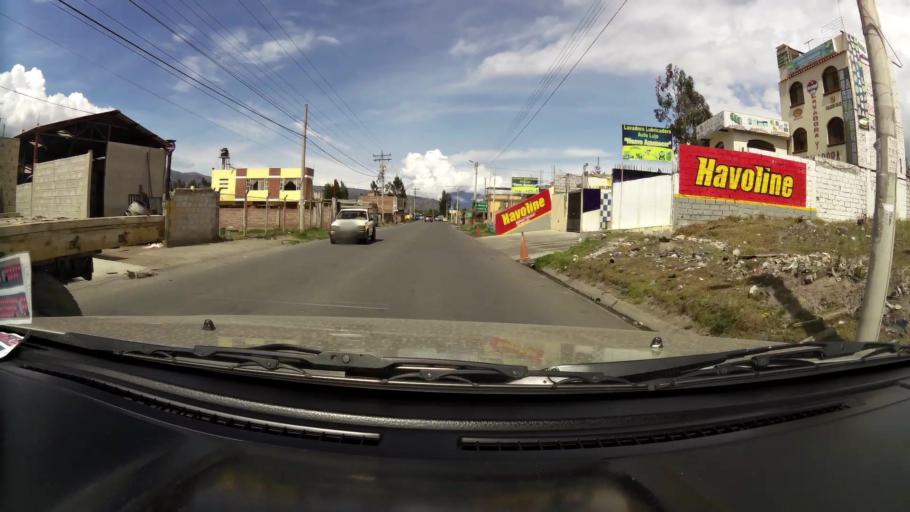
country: EC
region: Chimborazo
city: Riobamba
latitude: -1.6514
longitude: -78.6243
